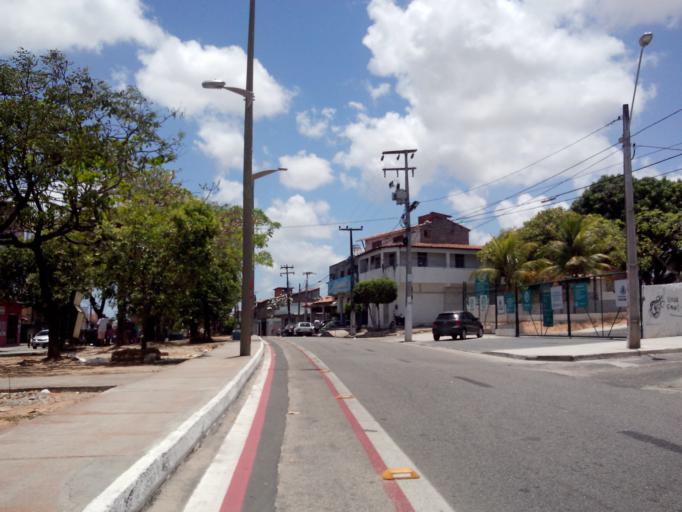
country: BR
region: Ceara
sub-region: Caucaia
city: Caucaia
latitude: -3.7710
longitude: -38.6029
